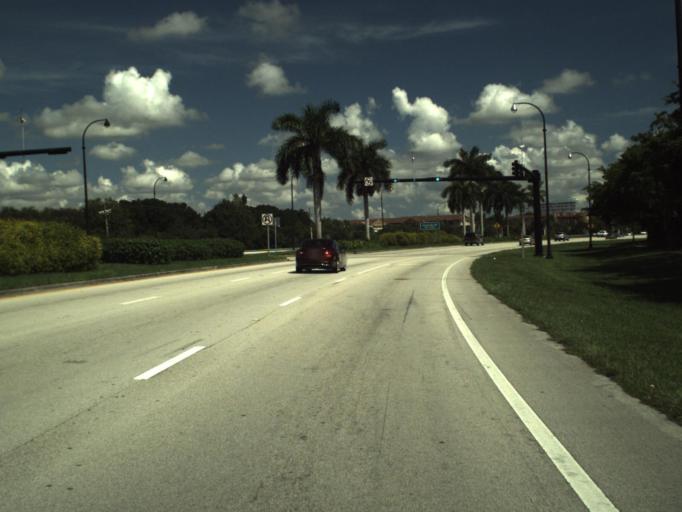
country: US
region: Florida
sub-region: Miami-Dade County
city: Country Club
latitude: 25.9899
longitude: -80.3106
